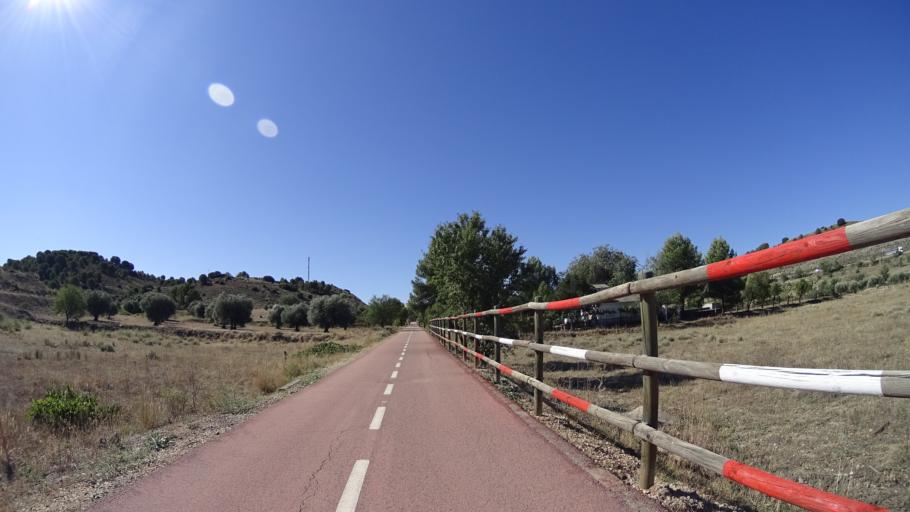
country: ES
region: Madrid
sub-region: Provincia de Madrid
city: Arganda
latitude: 40.2786
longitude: -3.4503
